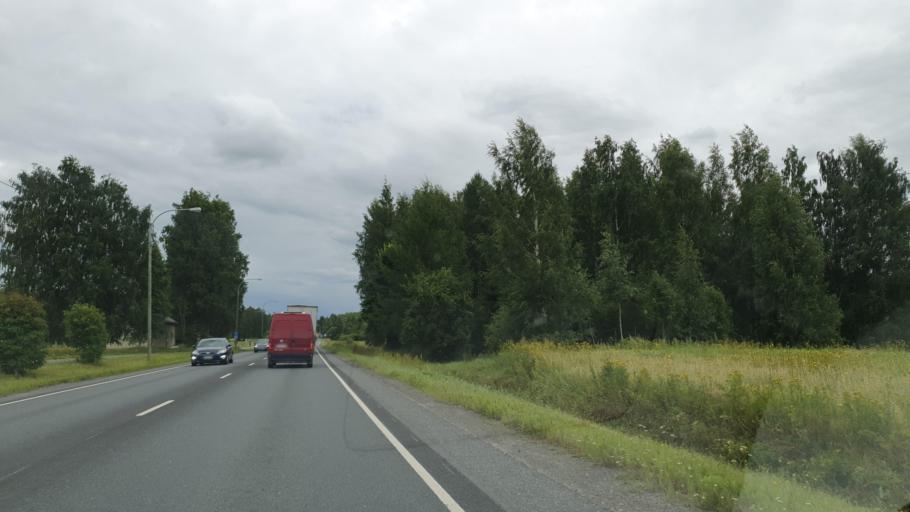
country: FI
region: Northern Savo
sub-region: Ylae-Savo
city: Lapinlahti
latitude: 63.4629
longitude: 27.3106
